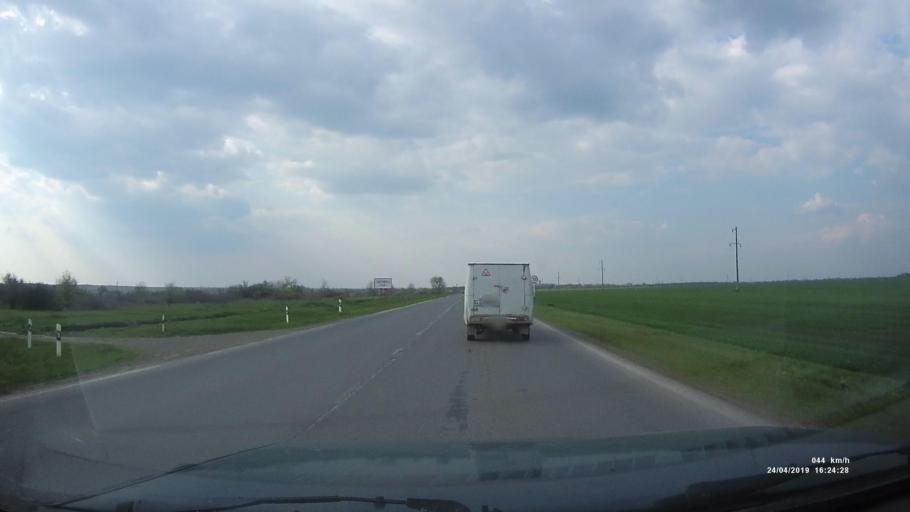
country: RU
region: Rostov
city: Orlovskiy
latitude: 46.8427
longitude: 42.0465
